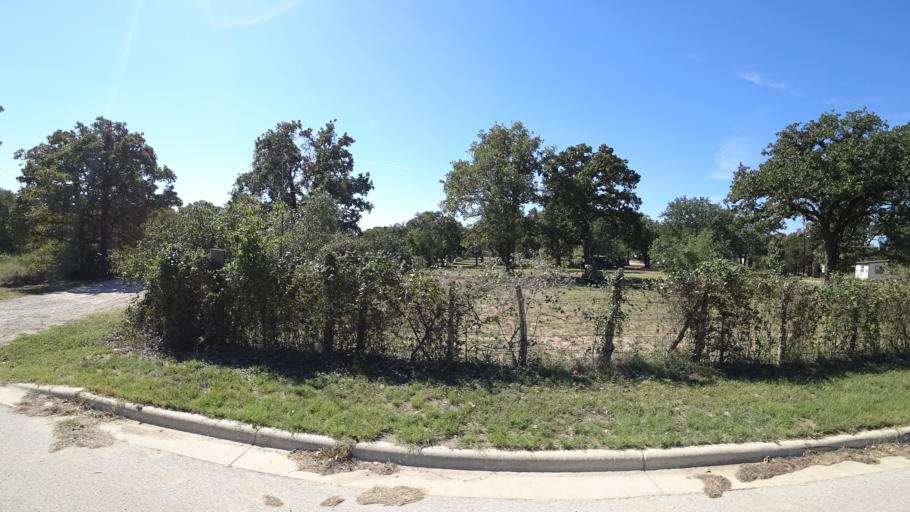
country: US
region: Texas
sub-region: Travis County
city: Hornsby Bend
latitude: 30.2756
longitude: -97.6099
